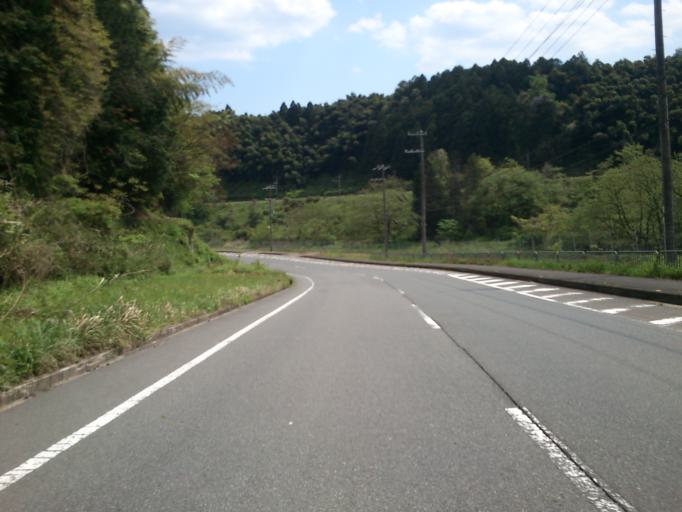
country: JP
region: Kyoto
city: Fukuchiyama
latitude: 35.3387
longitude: 134.9384
